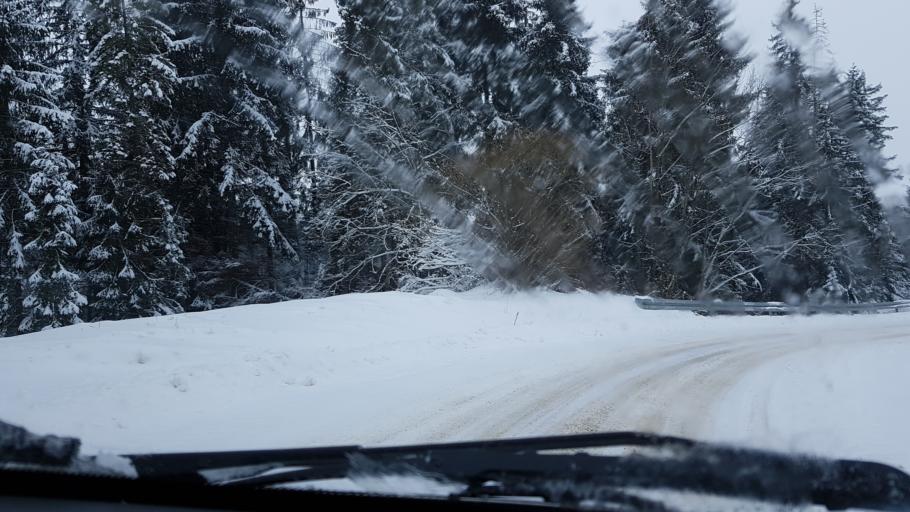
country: PL
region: Lesser Poland Voivodeship
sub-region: Powiat tatrzanski
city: Czarna Gora
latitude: 49.3564
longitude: 20.1604
